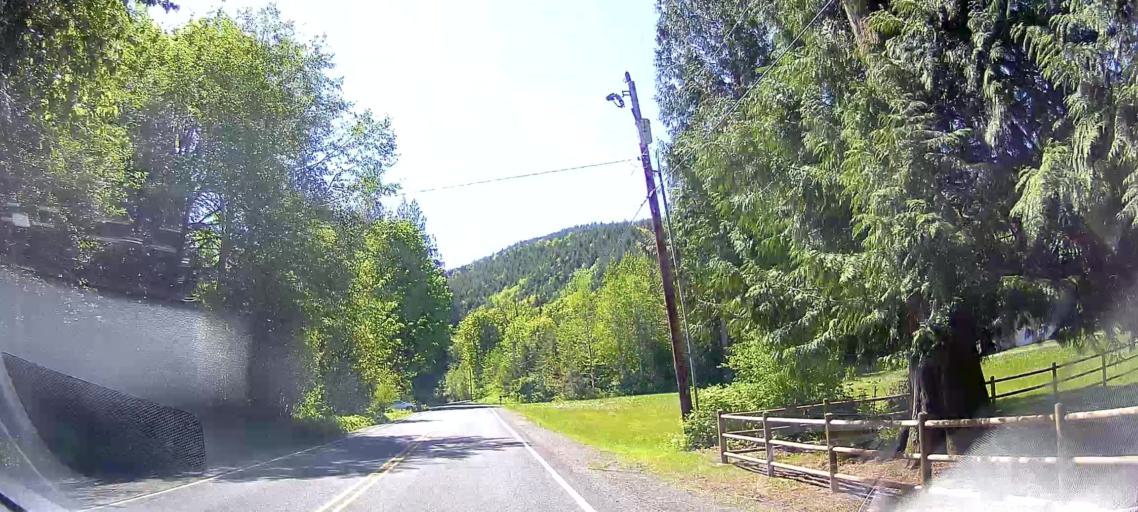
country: US
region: Washington
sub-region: Snohomish County
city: Darrington
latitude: 48.4858
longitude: -121.6549
